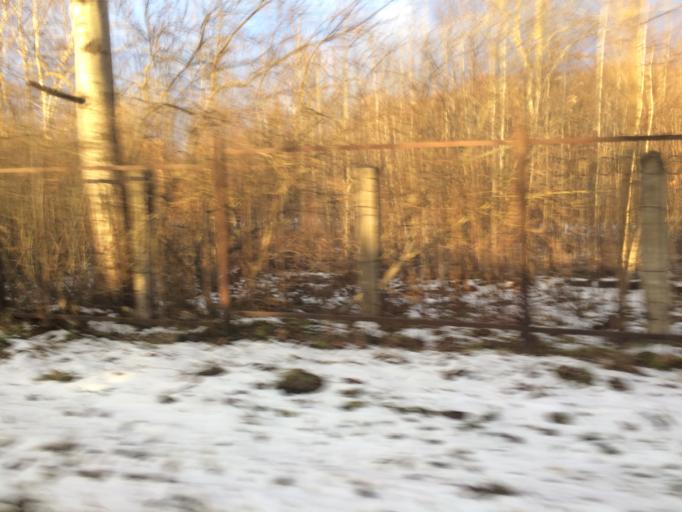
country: RU
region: Tula
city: Cherepet'
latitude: 54.1121
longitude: 36.3351
